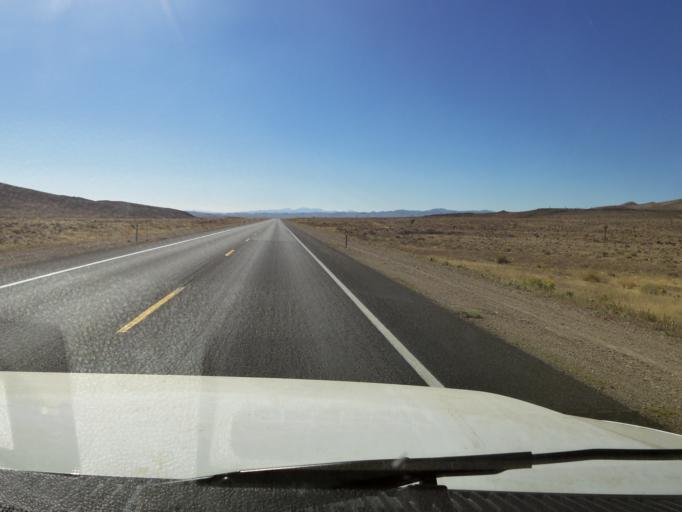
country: US
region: Nevada
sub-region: Esmeralda County
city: Goldfield
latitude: 37.5547
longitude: -117.1978
